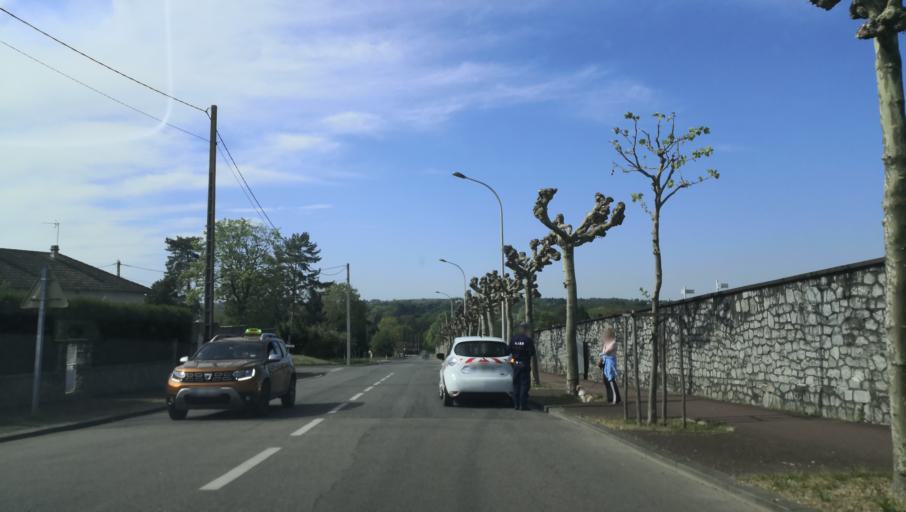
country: FR
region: Limousin
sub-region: Departement de la Haute-Vienne
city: Limoges
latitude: 45.8557
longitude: 1.2595
